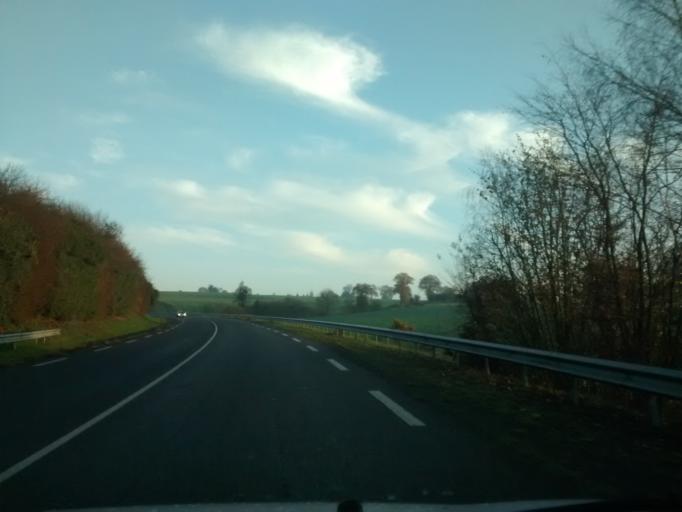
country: FR
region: Brittany
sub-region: Departement d'Ille-et-Vilaine
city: Chasne-sur-Illet
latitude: 48.2598
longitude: -1.5994
